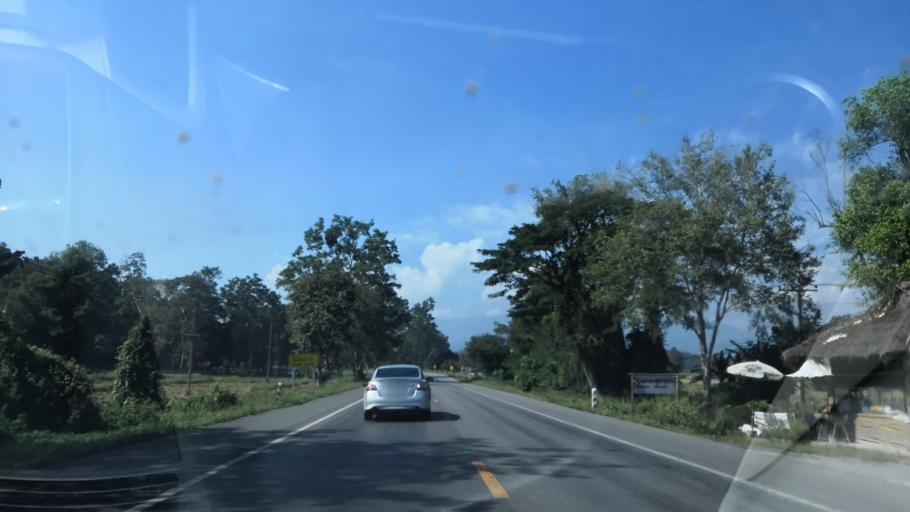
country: TH
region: Chiang Rai
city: Mae Lao
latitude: 19.7468
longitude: 99.6824
